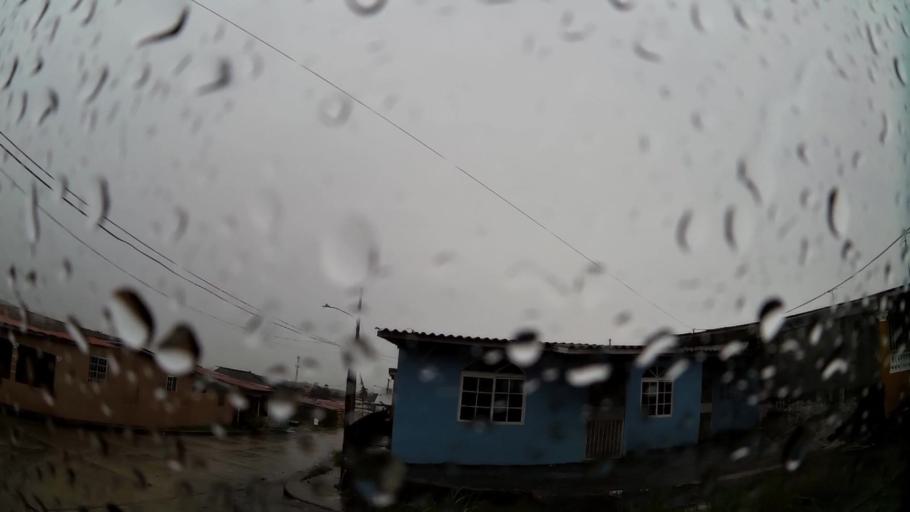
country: PA
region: Colon
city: Puerto Pilon
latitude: 9.3546
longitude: -79.7919
